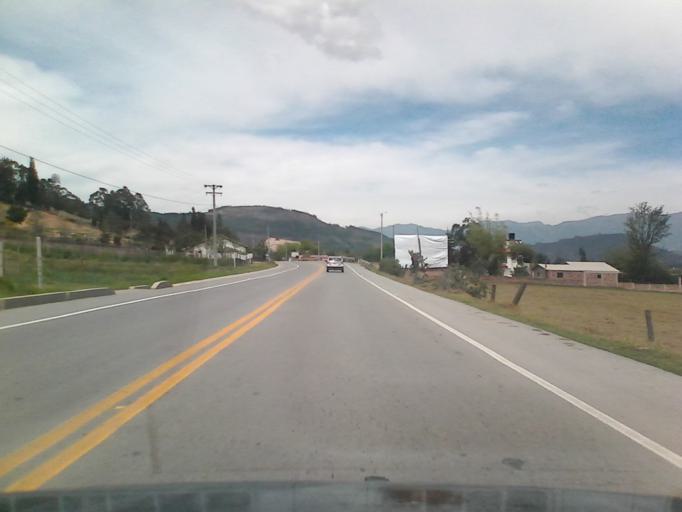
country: CO
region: Boyaca
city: Tibasosa
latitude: 5.7405
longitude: -72.9750
